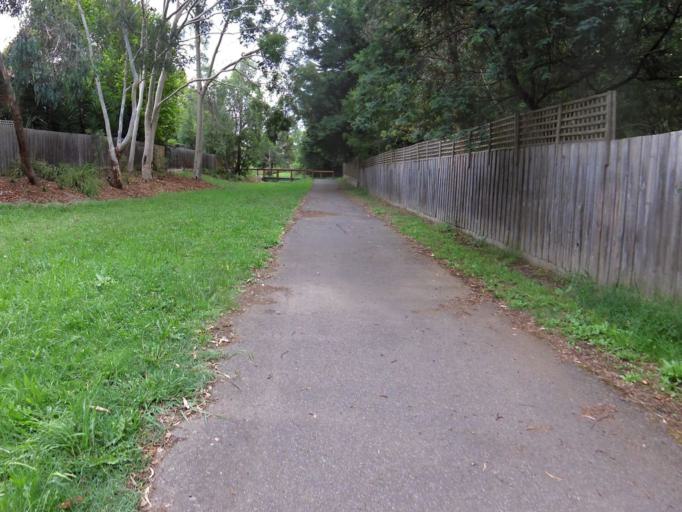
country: AU
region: Victoria
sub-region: Manningham
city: Donvale
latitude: -37.7750
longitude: 145.1846
